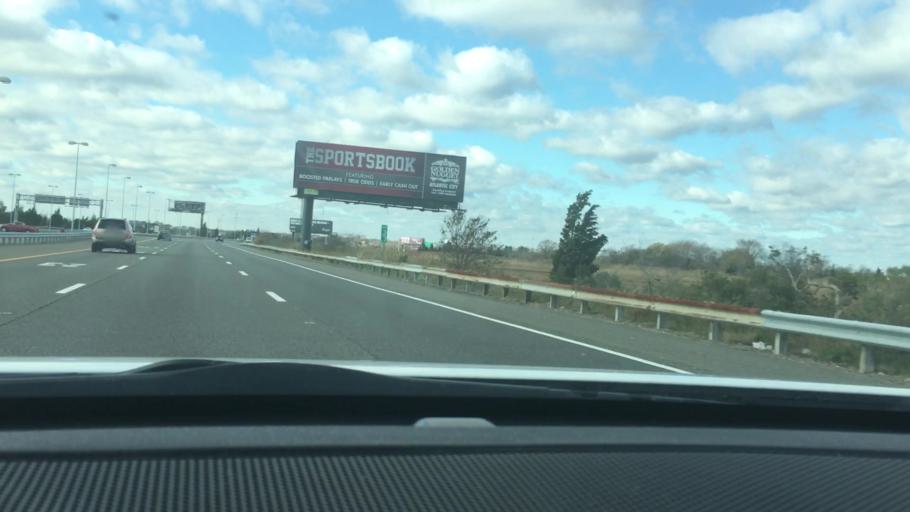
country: US
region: New Jersey
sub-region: Atlantic County
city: Pleasantville
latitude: 39.3851
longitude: -74.5019
